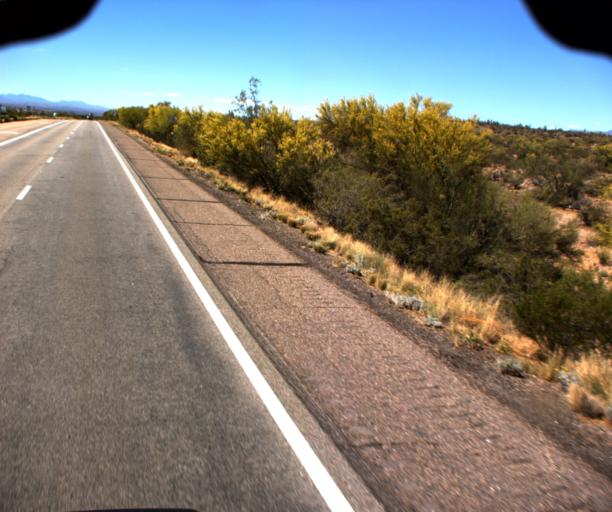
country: US
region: Arizona
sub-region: Yavapai County
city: Bagdad
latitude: 34.6518
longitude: -113.5726
